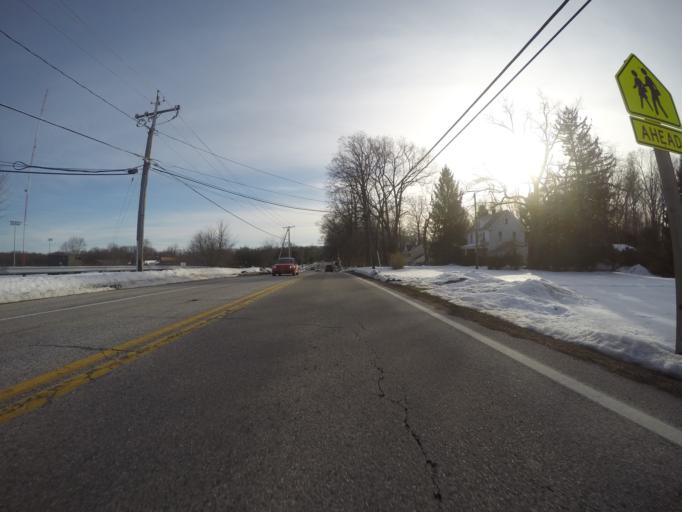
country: US
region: Maryland
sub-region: Baltimore County
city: Hunt Valley
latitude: 39.5151
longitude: -76.5604
